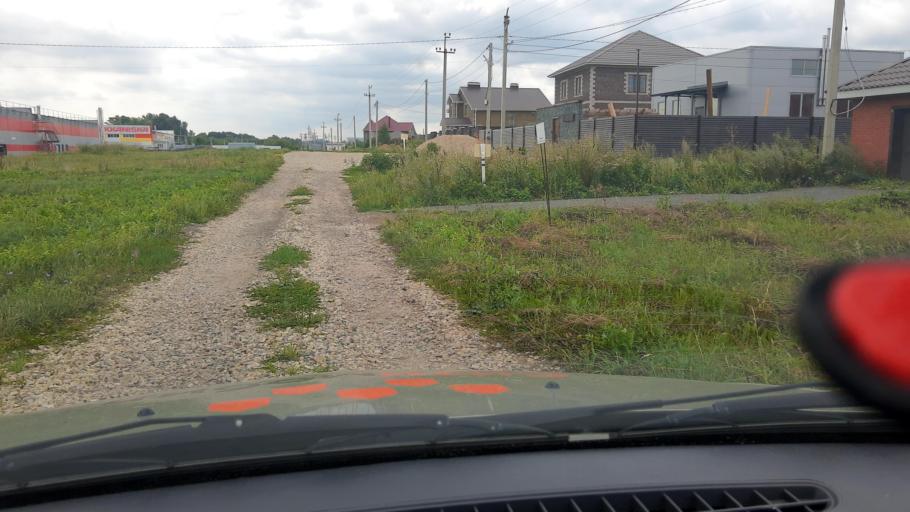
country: RU
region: Bashkortostan
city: Ufa
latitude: 54.6174
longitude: 55.9242
